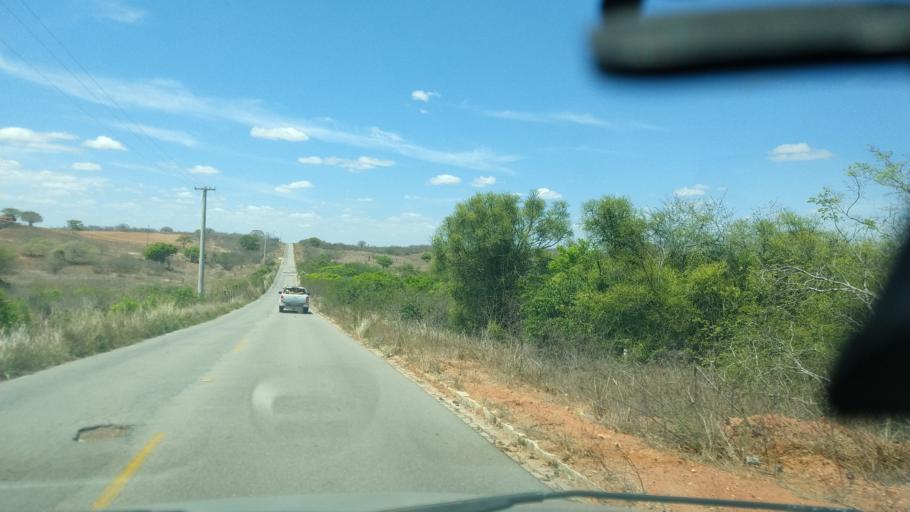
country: BR
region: Rio Grande do Norte
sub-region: Sao Paulo Do Potengi
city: Sao Paulo do Potengi
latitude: -5.9037
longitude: -35.6118
